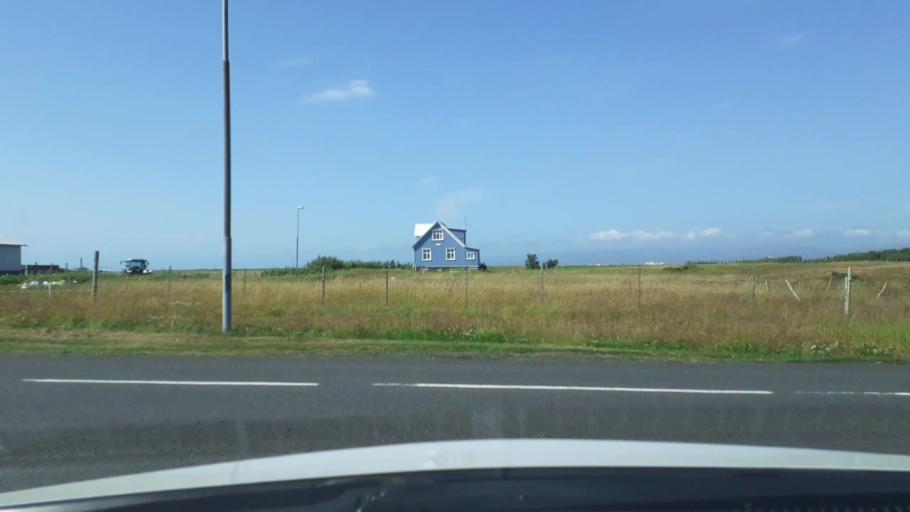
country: IS
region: South
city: Selfoss
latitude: 63.8415
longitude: -21.0525
